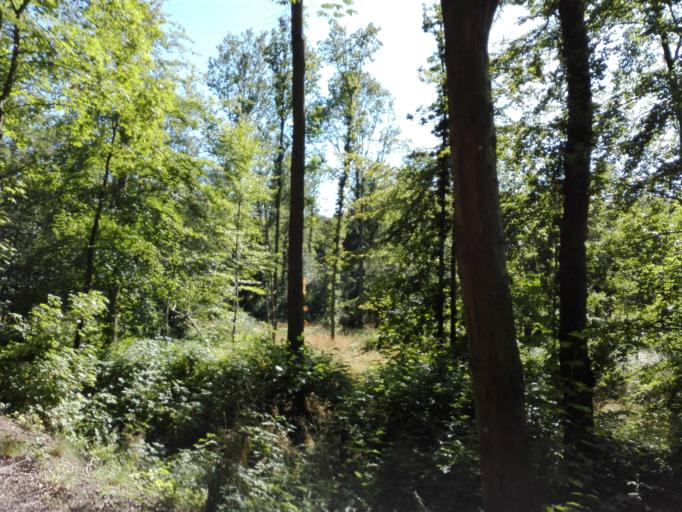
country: DK
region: Central Jutland
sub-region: Odder Kommune
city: Odder
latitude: 55.9690
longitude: 10.1215
